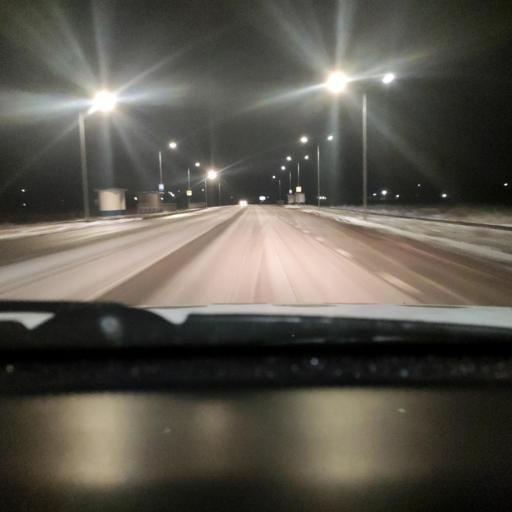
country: RU
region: Perm
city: Kultayevo
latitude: 57.8706
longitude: 55.8677
